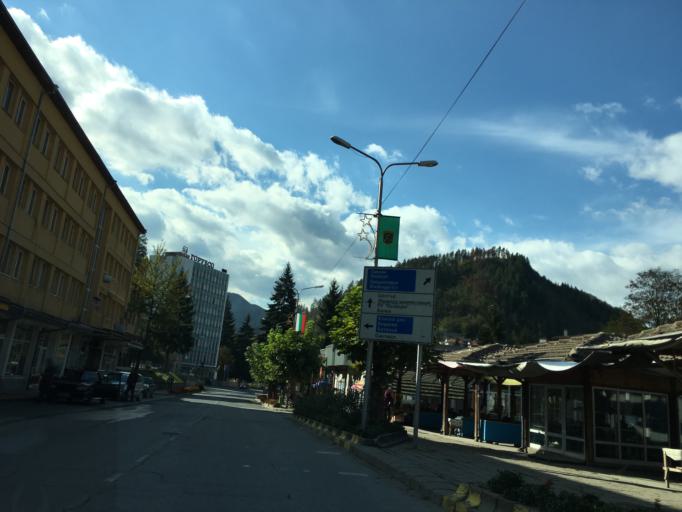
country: BG
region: Smolyan
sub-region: Obshtina Madan
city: Madan
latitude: 41.4986
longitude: 24.9421
